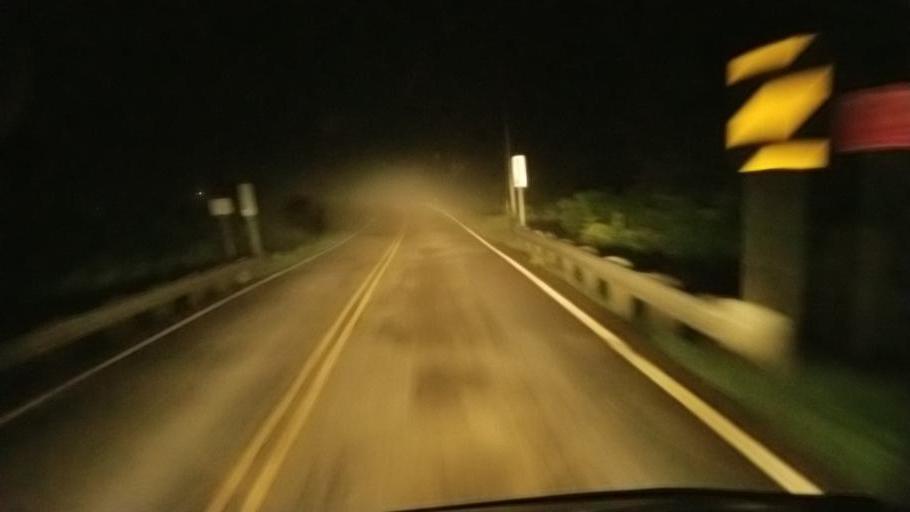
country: US
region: Ohio
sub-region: Coshocton County
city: Coshocton
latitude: 40.3559
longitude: -82.0209
